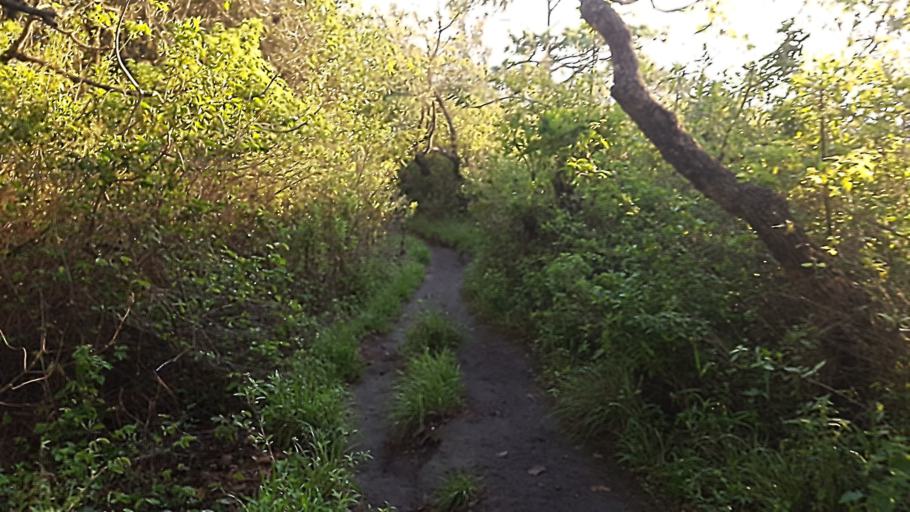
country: MX
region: Nayarit
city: Tepic
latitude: 21.5062
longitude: -104.9299
